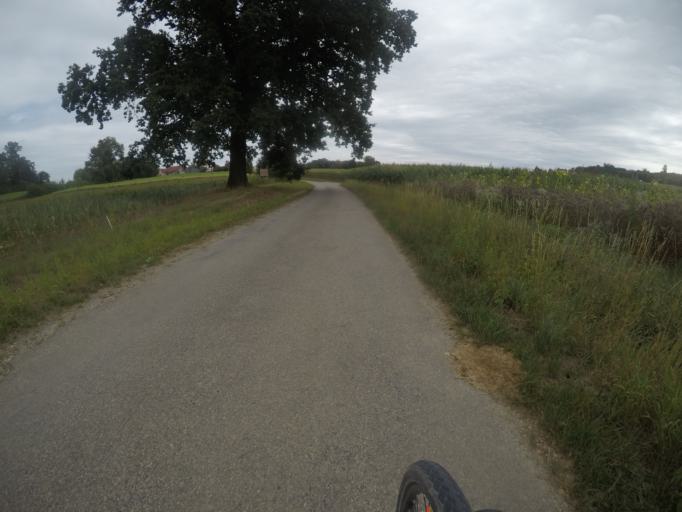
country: DE
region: Baden-Wuerttemberg
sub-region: Regierungsbezirk Stuttgart
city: Oberriexingen
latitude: 48.9074
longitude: 9.0180
